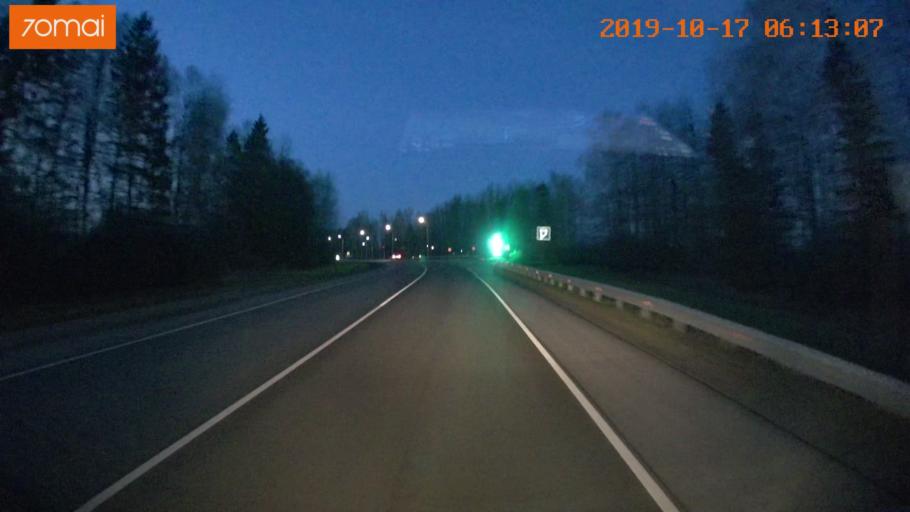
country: RU
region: Ivanovo
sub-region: Gorod Ivanovo
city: Ivanovo
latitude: 56.9027
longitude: 40.9382
